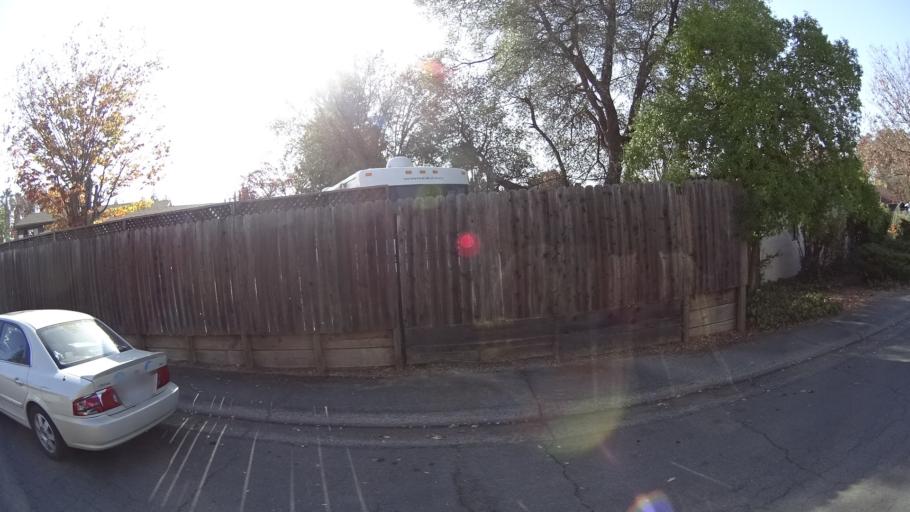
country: US
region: California
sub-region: Sacramento County
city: Citrus Heights
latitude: 38.6996
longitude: -121.2500
